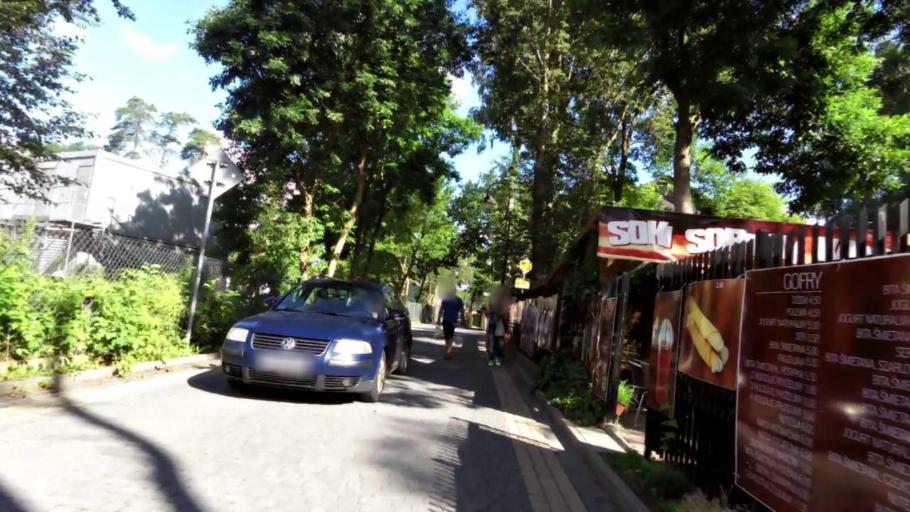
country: PL
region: West Pomeranian Voivodeship
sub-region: Powiat koszalinski
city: Mielno
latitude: 54.2629
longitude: 16.0630
